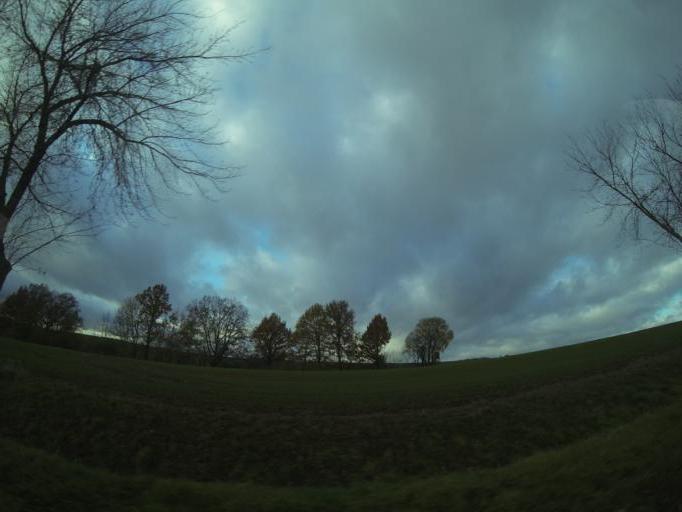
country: DE
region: Thuringia
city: Nobdenitz
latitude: 50.8598
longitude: 12.2829
